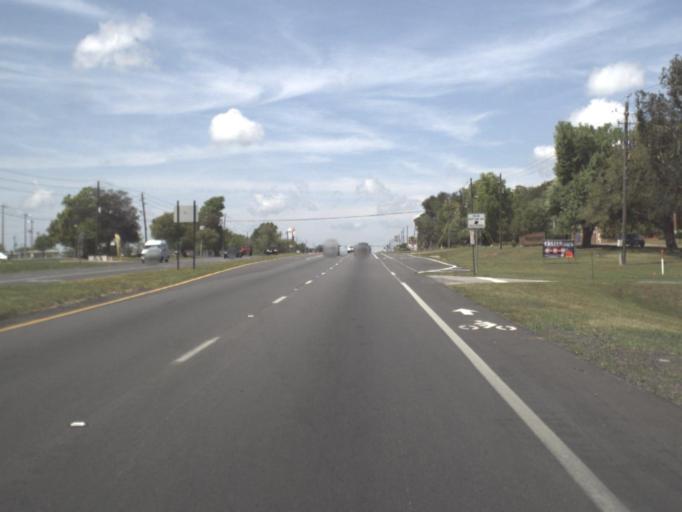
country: US
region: Florida
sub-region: Escambia County
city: Ensley
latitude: 30.5328
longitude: -87.2479
